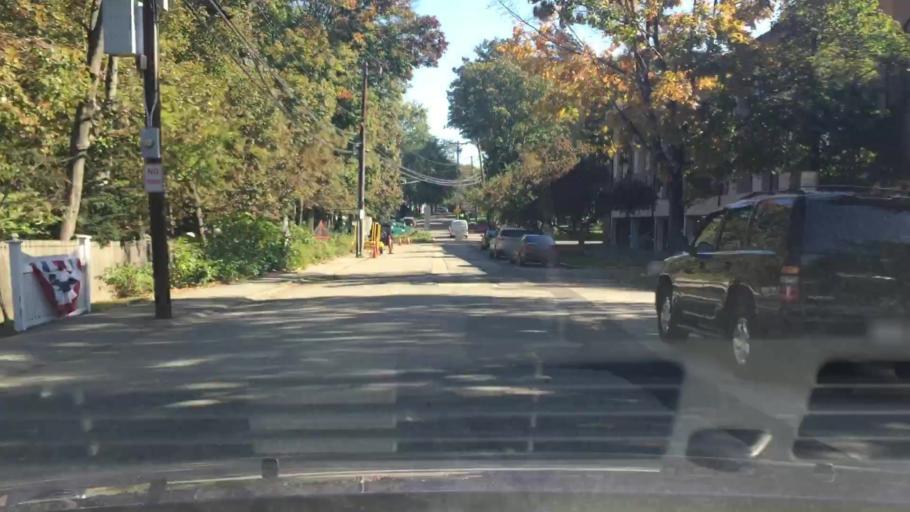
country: US
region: Massachusetts
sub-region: Essex County
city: North Andover
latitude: 42.6936
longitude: -71.1183
